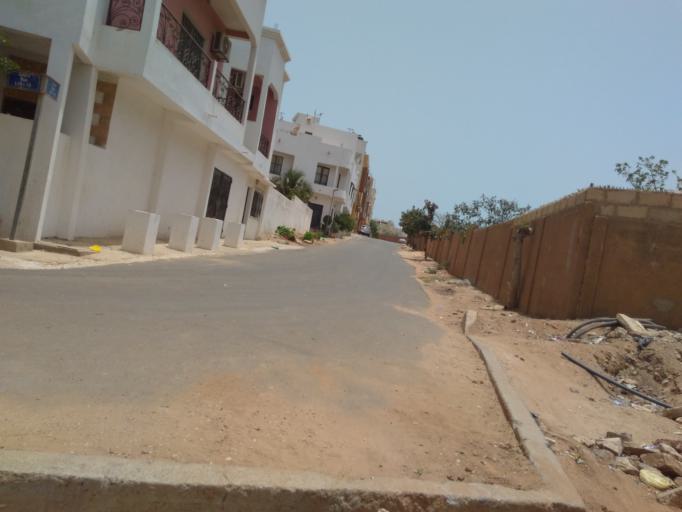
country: SN
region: Dakar
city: Grand Dakar
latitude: 14.7324
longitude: -17.4714
